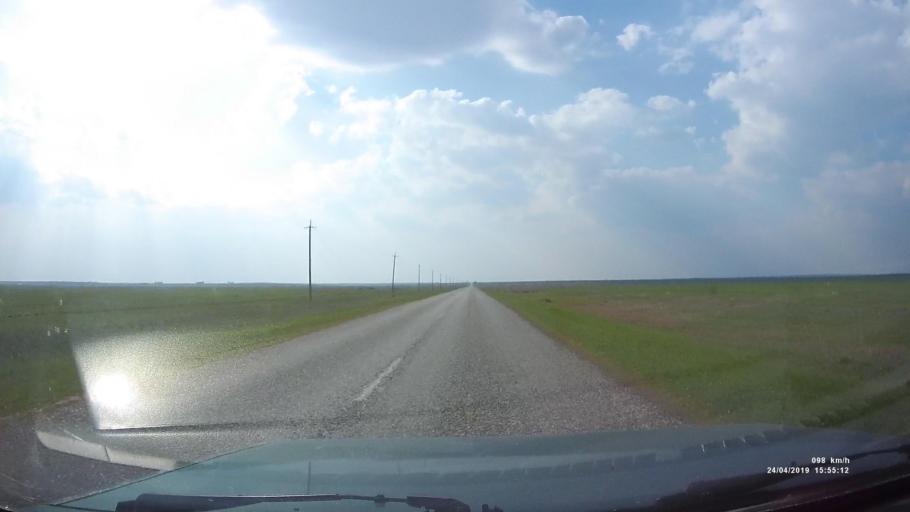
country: RU
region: Kalmykiya
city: Yashalta
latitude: 46.5887
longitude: 42.5540
